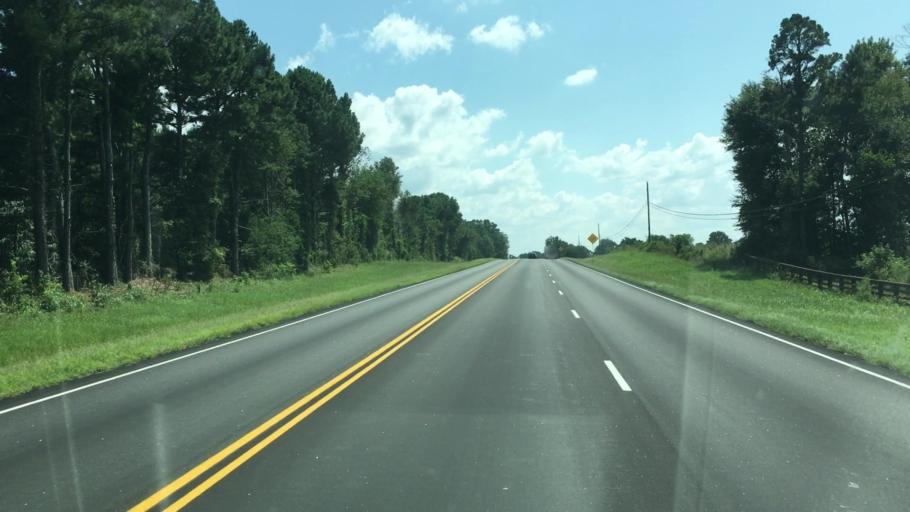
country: US
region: Georgia
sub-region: Morgan County
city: Madison
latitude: 33.7082
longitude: -83.4423
